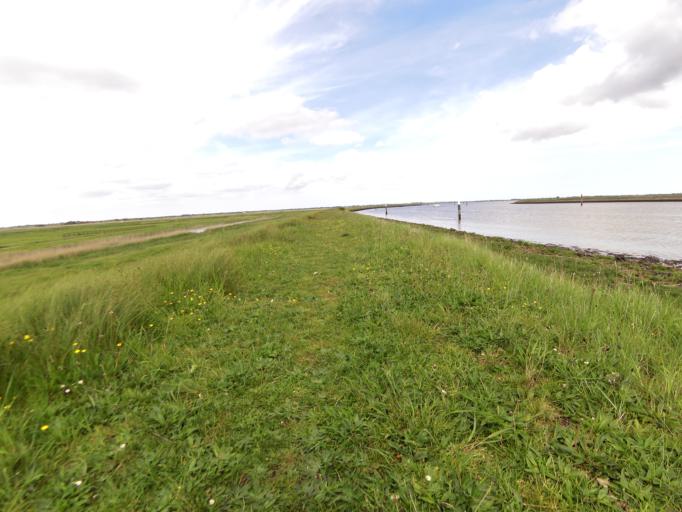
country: GB
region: England
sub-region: Norfolk
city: Great Yarmouth
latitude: 52.5920
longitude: 1.6467
